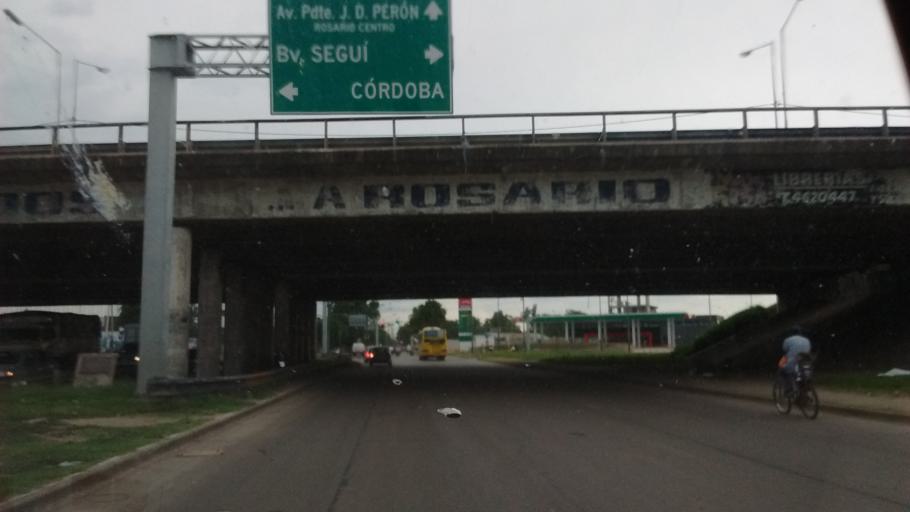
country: AR
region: Santa Fe
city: Perez
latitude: -32.9709
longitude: -60.7173
